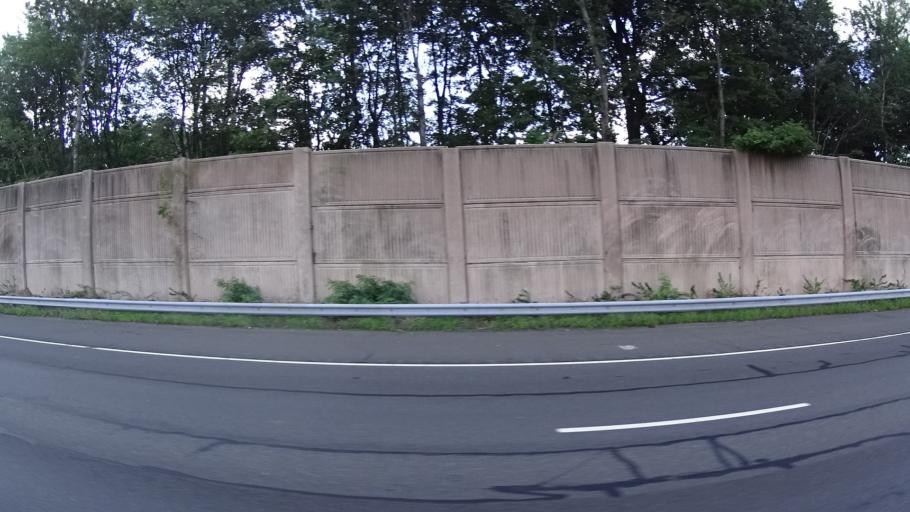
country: US
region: New Jersey
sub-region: Essex County
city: Maplewood
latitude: 40.7142
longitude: -74.2884
